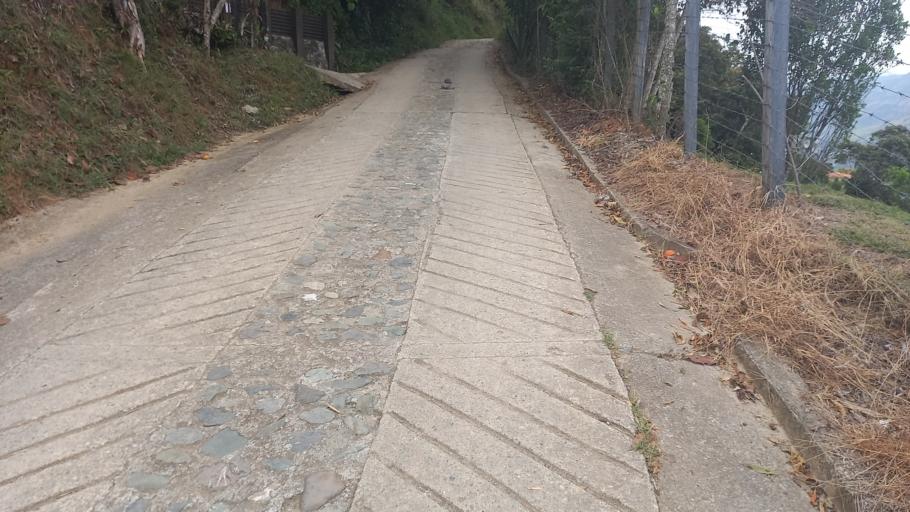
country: CO
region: Antioquia
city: Santa Barbara
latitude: 5.8335
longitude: -75.5756
